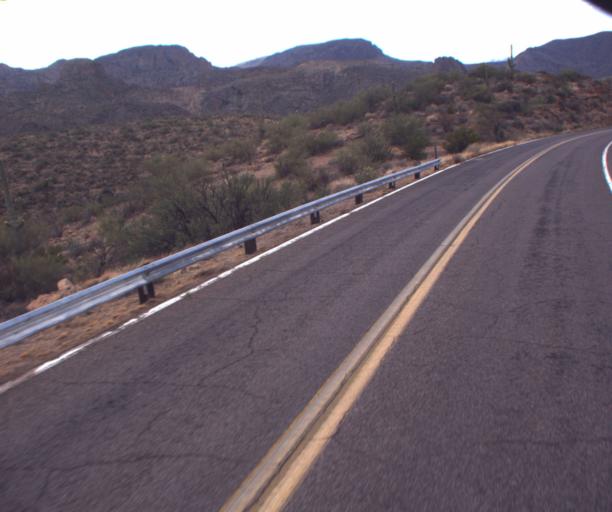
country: US
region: Arizona
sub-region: Pinal County
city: Apache Junction
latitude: 33.5352
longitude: -111.3475
